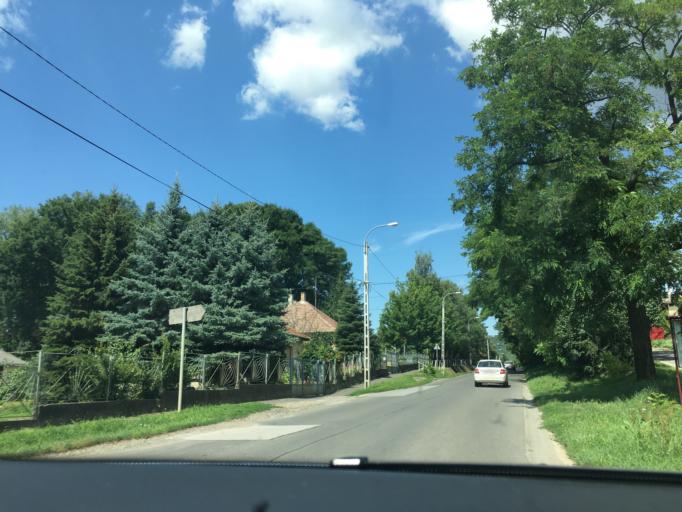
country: HU
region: Borsod-Abauj-Zemplen
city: Tarcal
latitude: 48.1697
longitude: 21.3611
